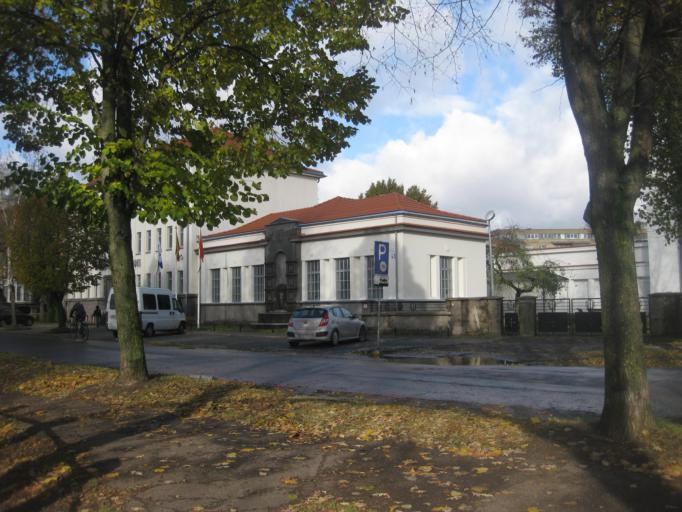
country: LT
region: Kauno apskritis
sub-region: Kaunas
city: Kaunas
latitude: 54.9024
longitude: 23.9270
